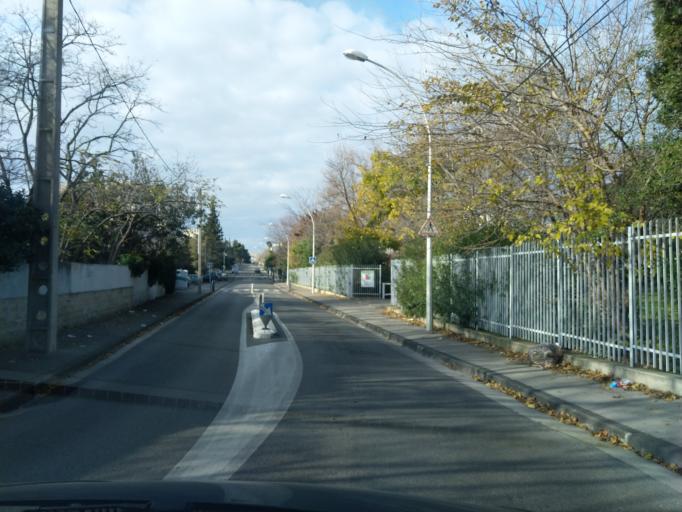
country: FR
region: Provence-Alpes-Cote d'Azur
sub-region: Departement des Bouches-du-Rhone
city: Marseille 04
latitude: 43.2981
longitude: 5.4147
